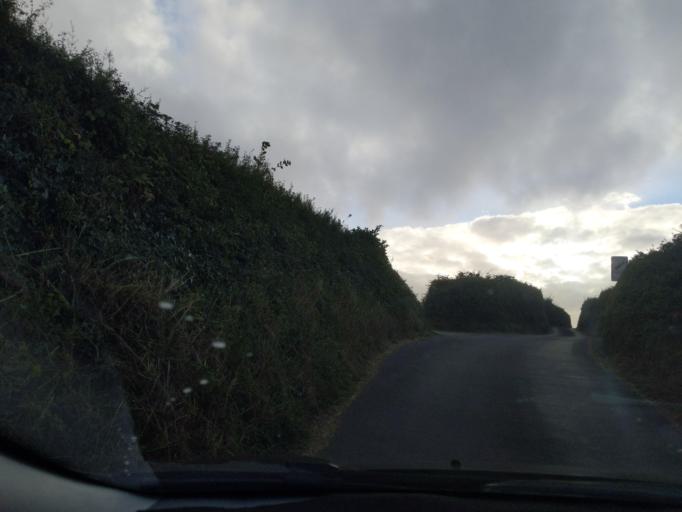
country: GB
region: England
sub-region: Devon
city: Salcombe
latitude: 50.2304
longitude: -3.8064
